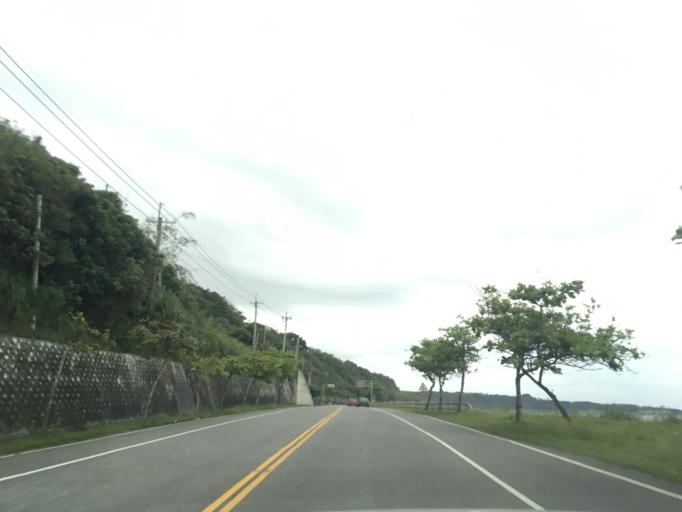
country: TW
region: Taiwan
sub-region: Taitung
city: Taitung
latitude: 23.2976
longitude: 121.4371
